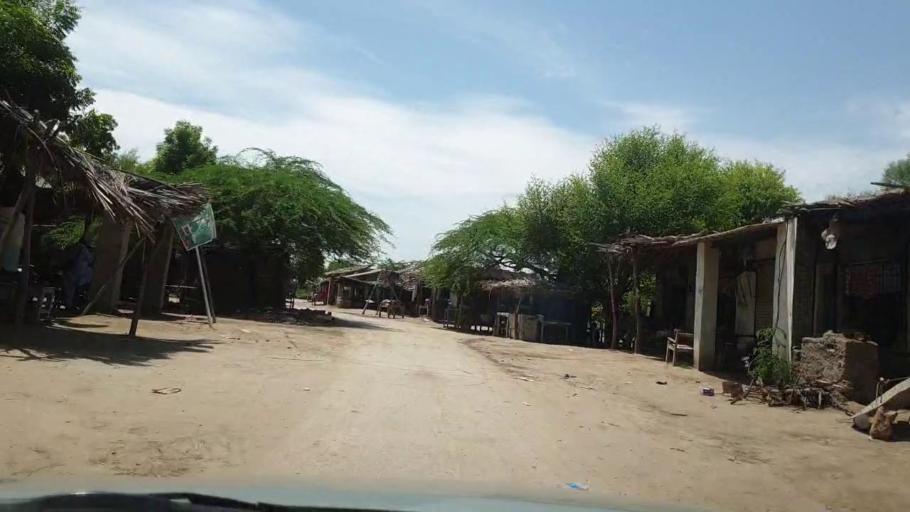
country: PK
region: Sindh
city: Bozdar
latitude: 27.0334
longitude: 68.9575
